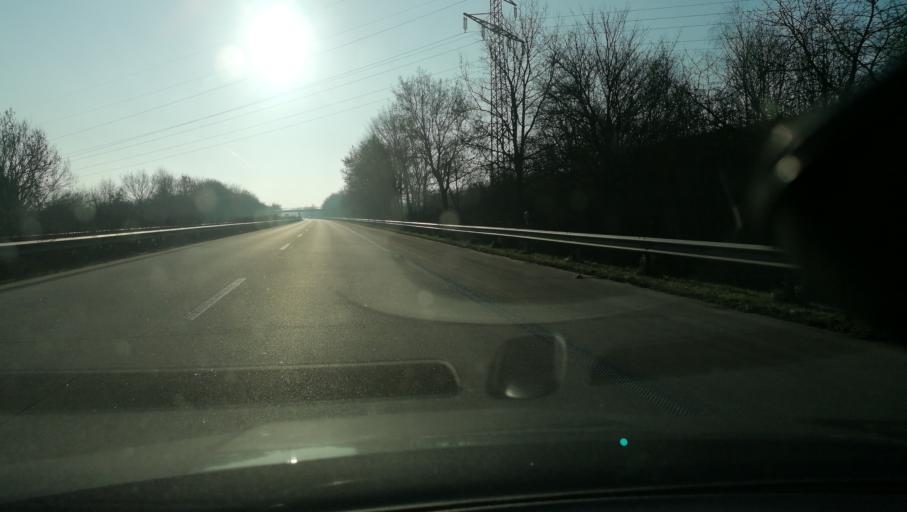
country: DE
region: Schleswig-Holstein
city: Kolln-Reisiek
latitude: 53.7605
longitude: 9.7079
